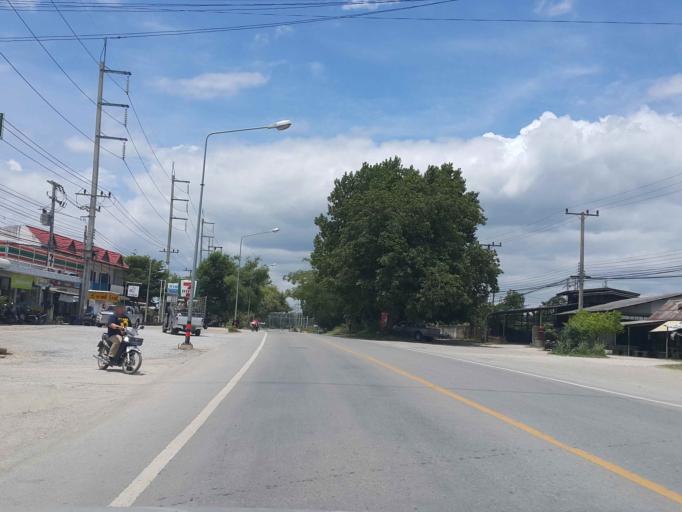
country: TH
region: Lamphun
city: Ban Hong
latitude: 18.3366
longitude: 98.8174
